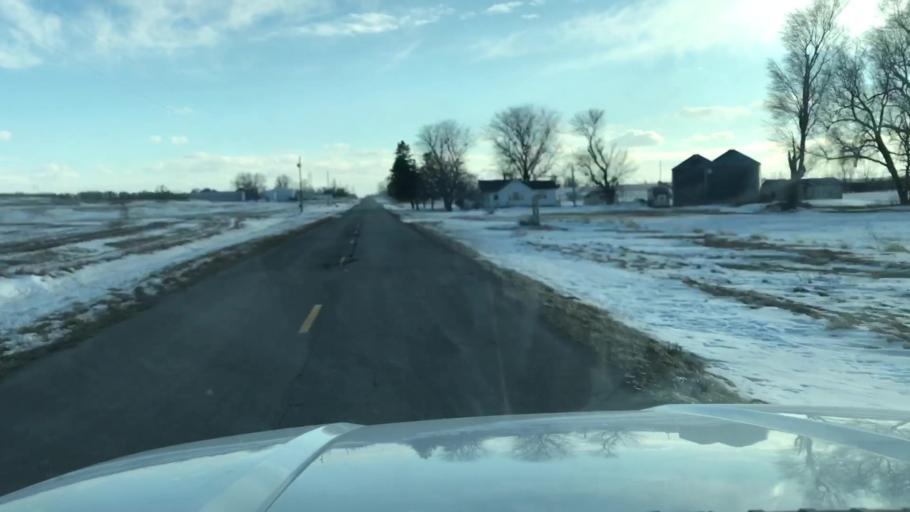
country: US
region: Missouri
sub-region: Holt County
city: Oregon
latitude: 40.1182
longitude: -95.0226
